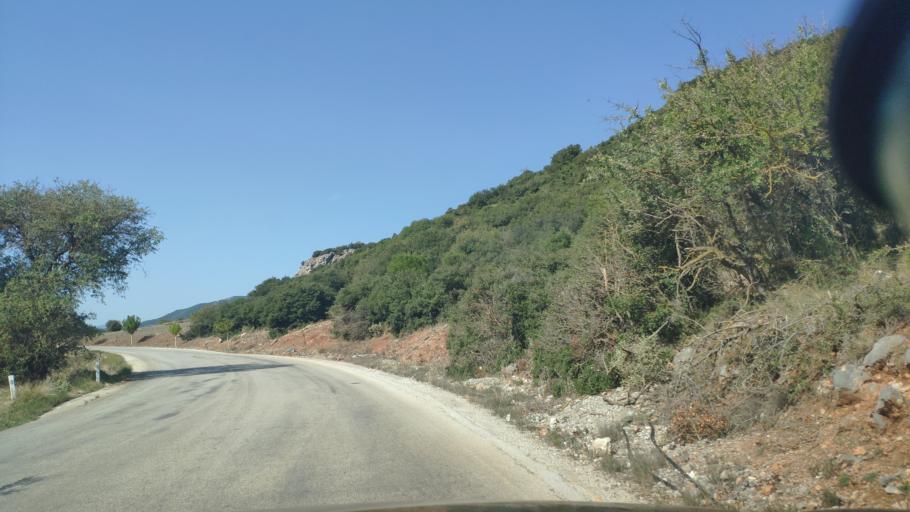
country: GR
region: Peloponnese
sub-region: Nomos Korinthias
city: Nemea
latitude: 37.8897
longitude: 22.5073
